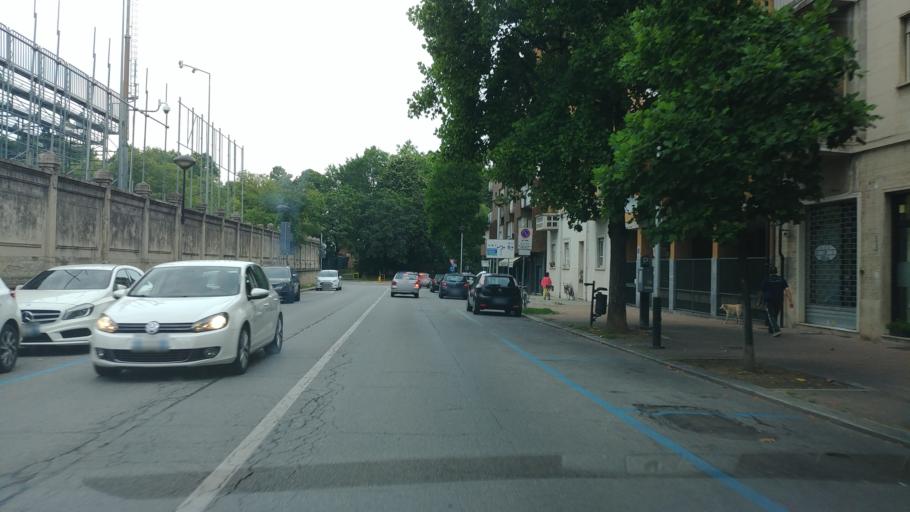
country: IT
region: Piedmont
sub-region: Provincia di Cuneo
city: Cuneo
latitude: 44.3836
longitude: 7.5351
